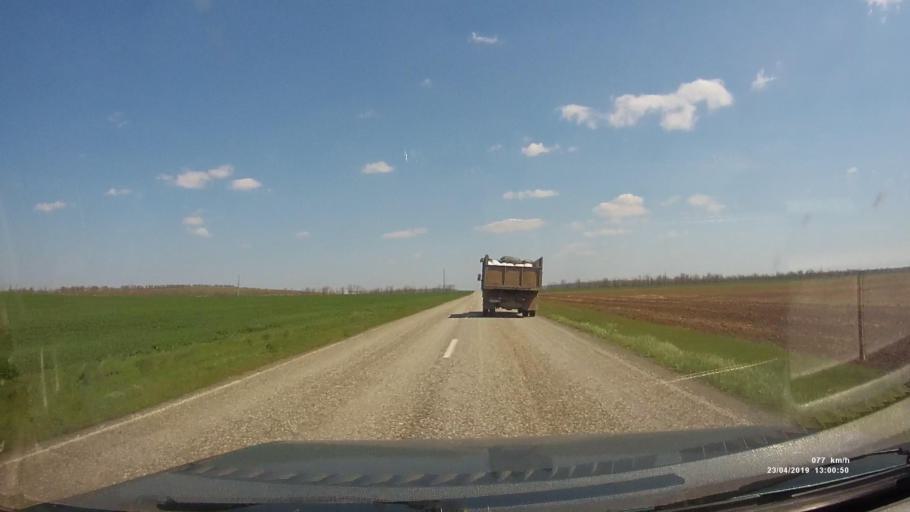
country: RU
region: Kalmykiya
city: Yashalta
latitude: 46.6040
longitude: 42.6413
